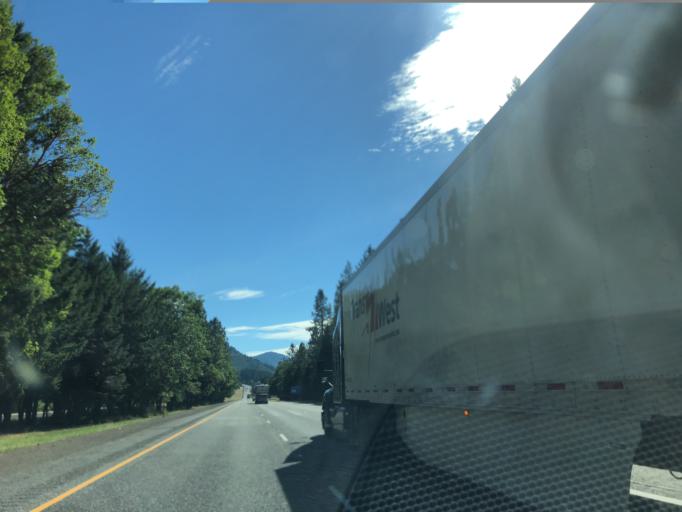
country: US
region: Oregon
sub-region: Douglas County
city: Canyonville
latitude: 42.7554
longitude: -123.3556
